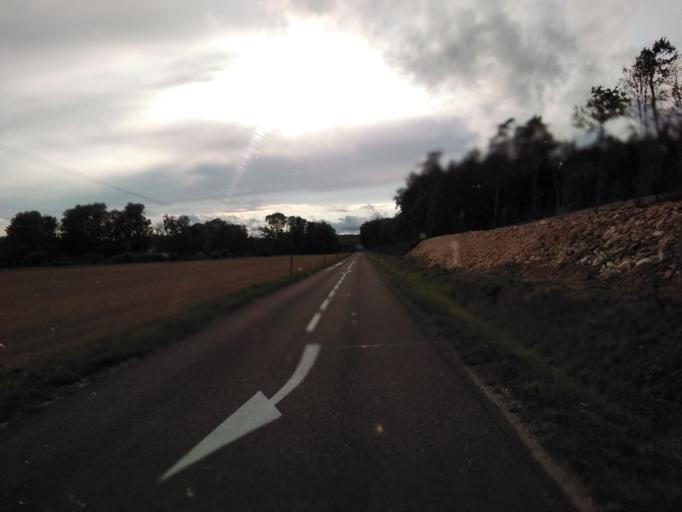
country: FR
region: Champagne-Ardenne
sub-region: Departement de l'Aube
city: Les Riceys
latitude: 47.9448
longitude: 4.3720
